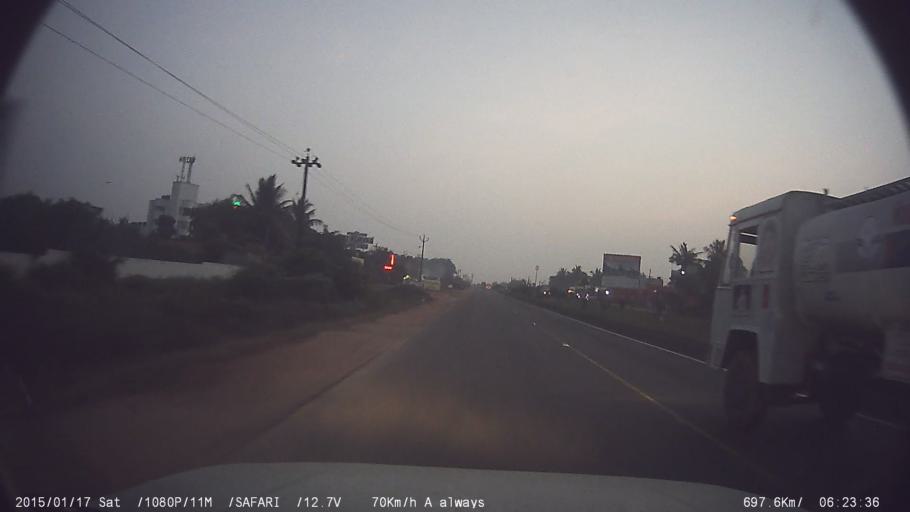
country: IN
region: Tamil Nadu
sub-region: Kancheepuram
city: Sriperumbudur
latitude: 12.9124
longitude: 79.8525
